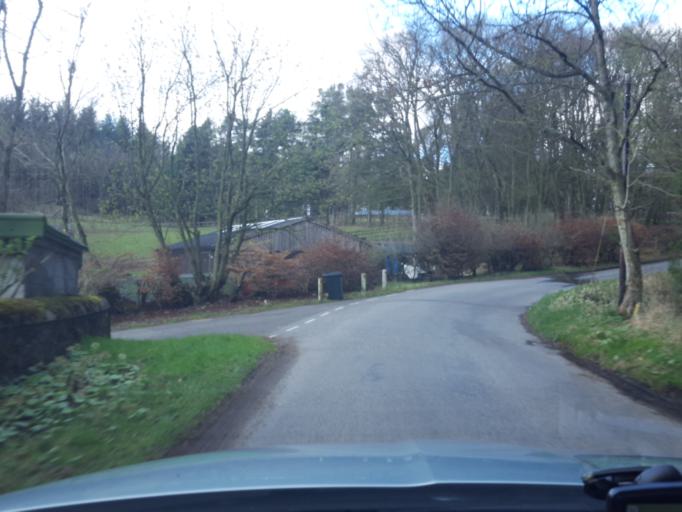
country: GB
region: Scotland
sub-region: Perth and Kinross
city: Scone
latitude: 56.3952
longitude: -3.3875
